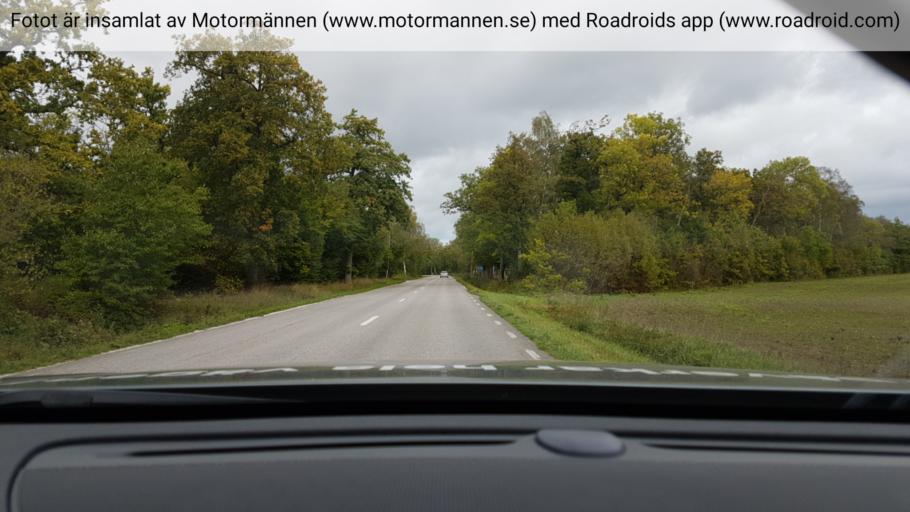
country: SE
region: Gotland
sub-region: Gotland
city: Klintehamn
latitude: 57.4256
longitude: 18.3656
